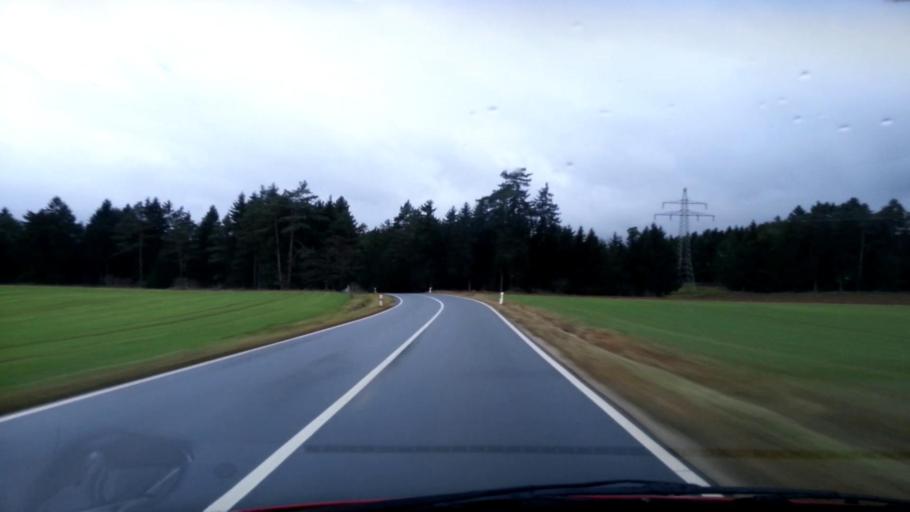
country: DE
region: Bavaria
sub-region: Upper Franconia
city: Konigsfeld
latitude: 49.9401
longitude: 11.2010
